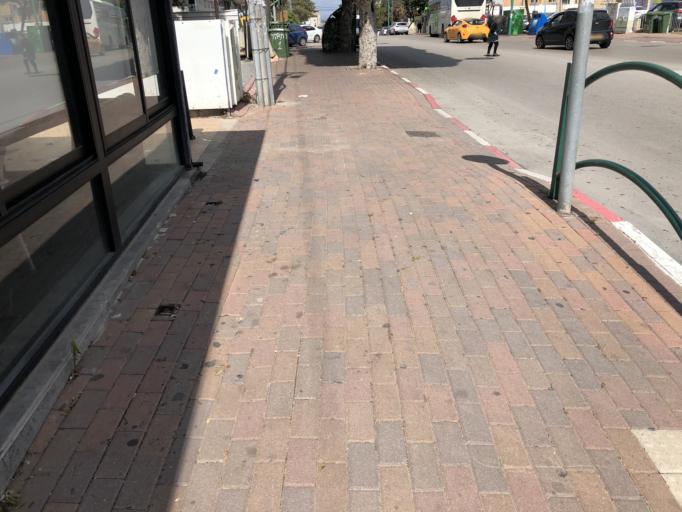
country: IL
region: Haifa
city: Hadera
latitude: 32.4373
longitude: 34.9171
